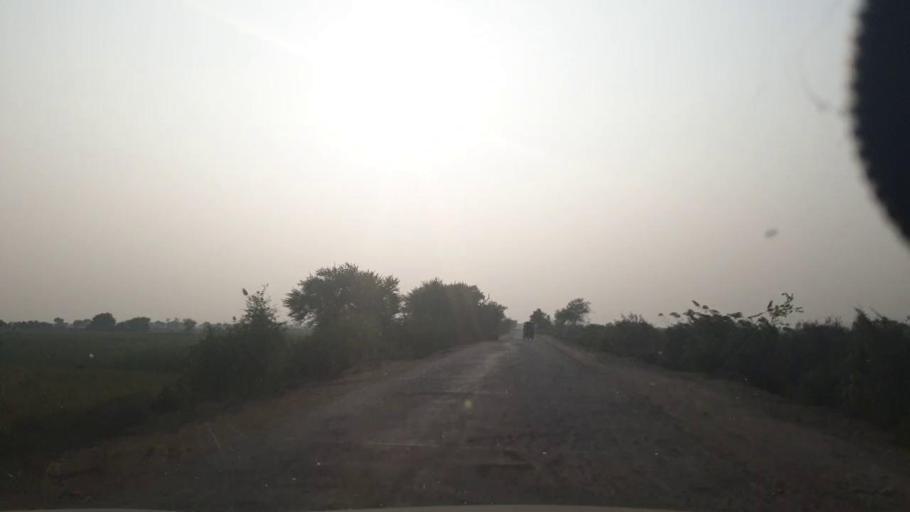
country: PK
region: Sindh
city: Bulri
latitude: 24.8513
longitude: 68.3502
